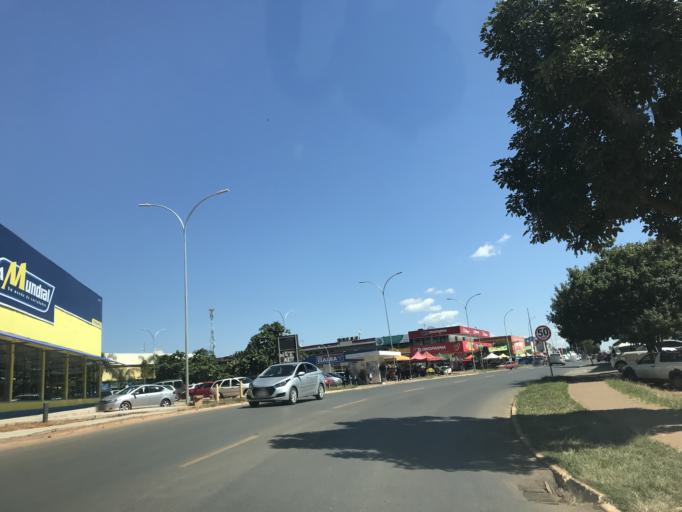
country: BR
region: Federal District
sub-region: Brasilia
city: Brasilia
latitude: -15.6504
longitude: -47.7885
